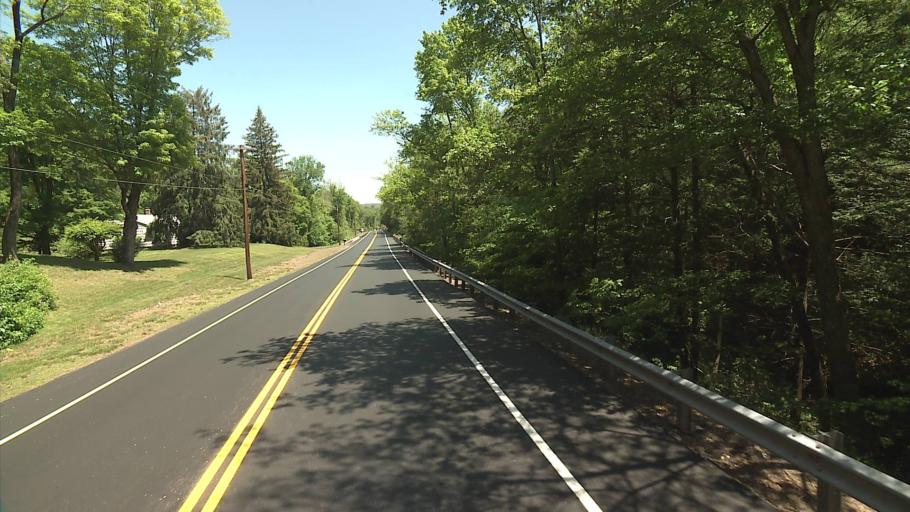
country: US
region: Connecticut
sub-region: Tolland County
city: Crystal Lake
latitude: 41.9643
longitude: -72.3638
